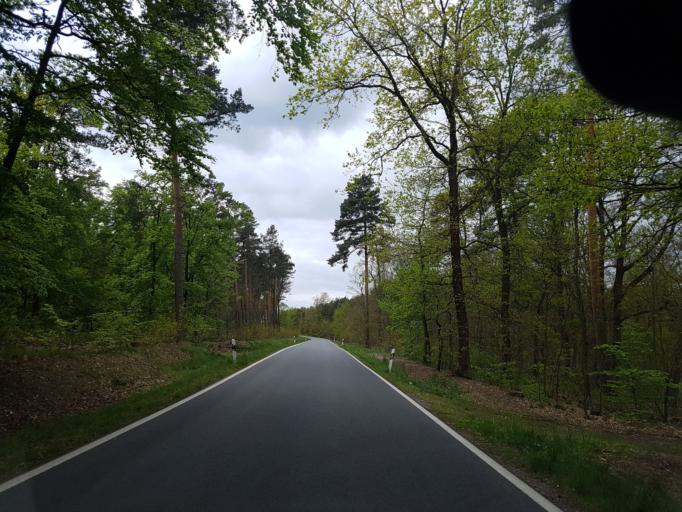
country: DE
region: Brandenburg
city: Altdobern
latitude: 51.6526
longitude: 13.9910
